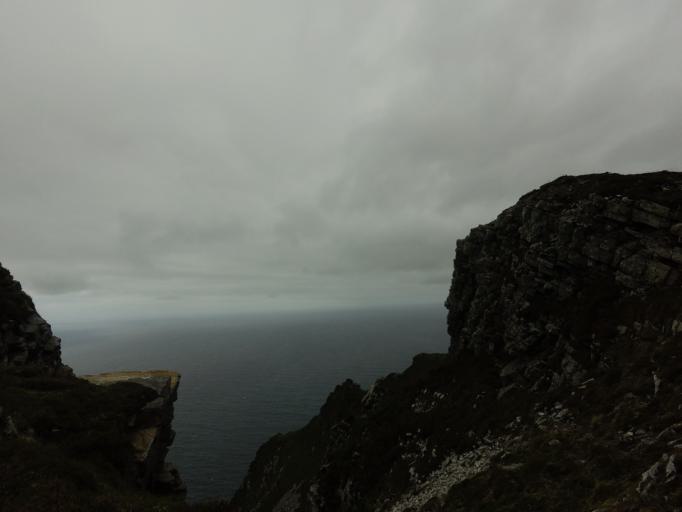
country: IE
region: Ulster
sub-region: County Donegal
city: Killybegs
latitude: 54.6462
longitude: -8.6888
